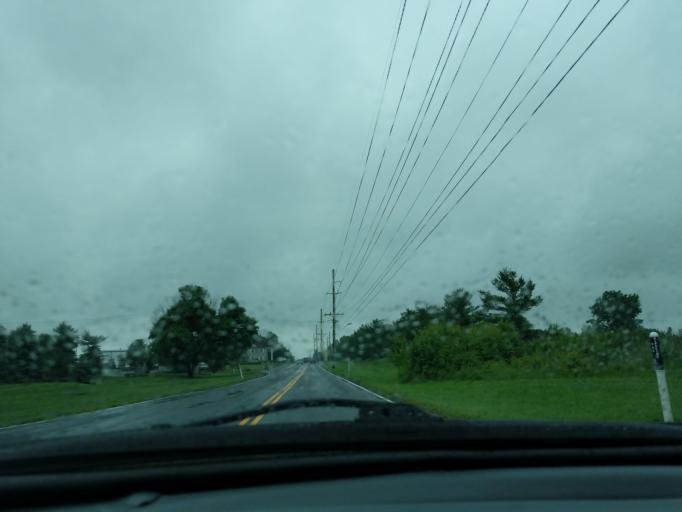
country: US
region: Indiana
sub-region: Hamilton County
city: Noblesville
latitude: 40.0827
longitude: -86.0334
